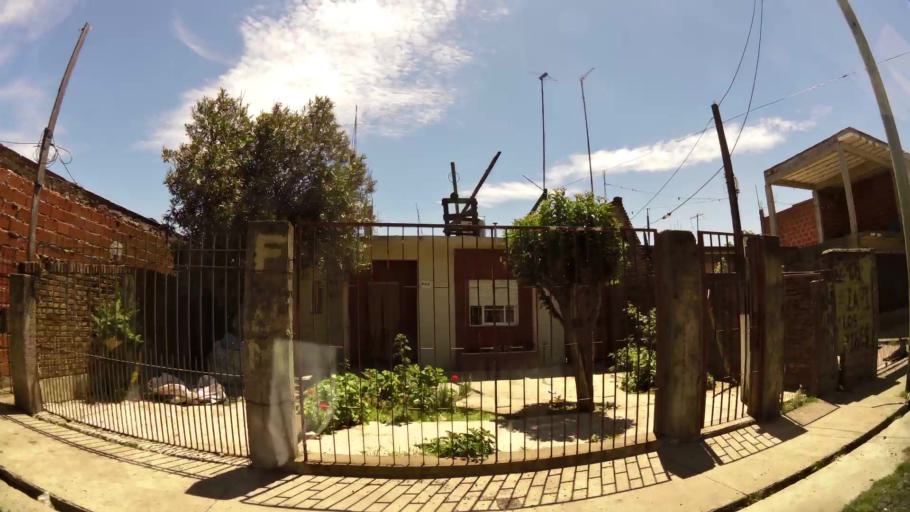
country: AR
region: Buenos Aires
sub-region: Partido de Lanus
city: Lanus
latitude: -34.7251
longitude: -58.3298
